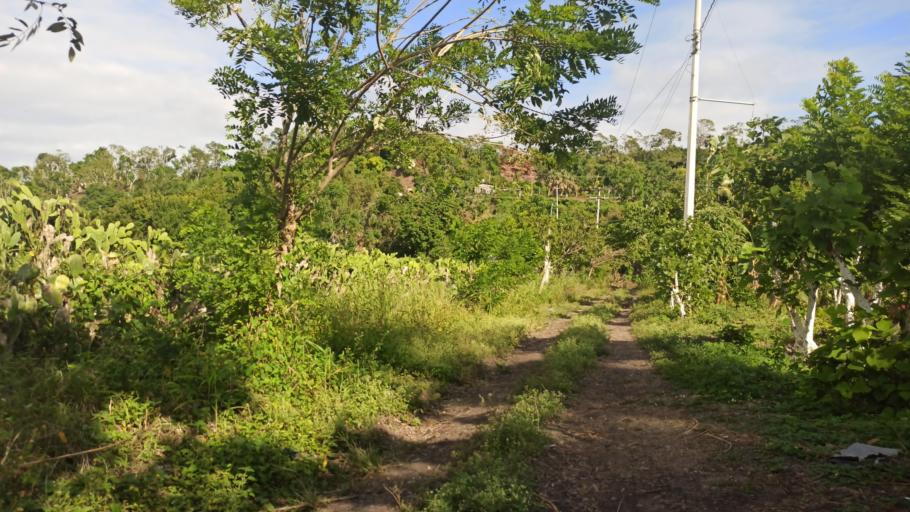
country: MX
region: Veracruz
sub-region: Papantla
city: Residencial Tajin
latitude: 20.6452
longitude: -97.3618
